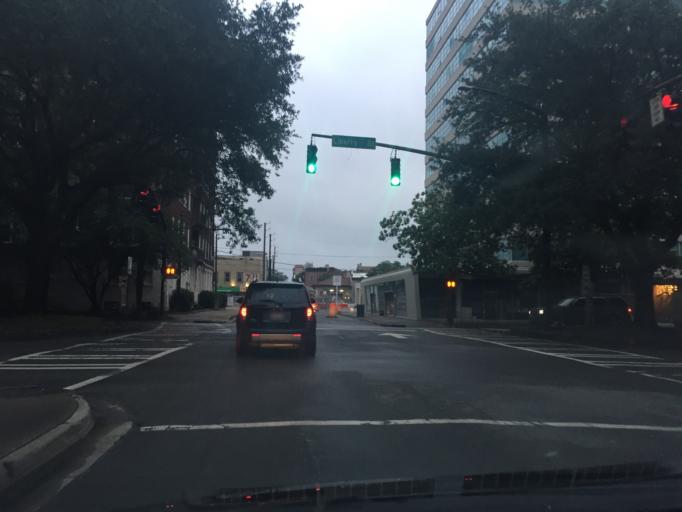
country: US
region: Georgia
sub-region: Chatham County
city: Savannah
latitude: 32.0742
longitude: -81.0925
